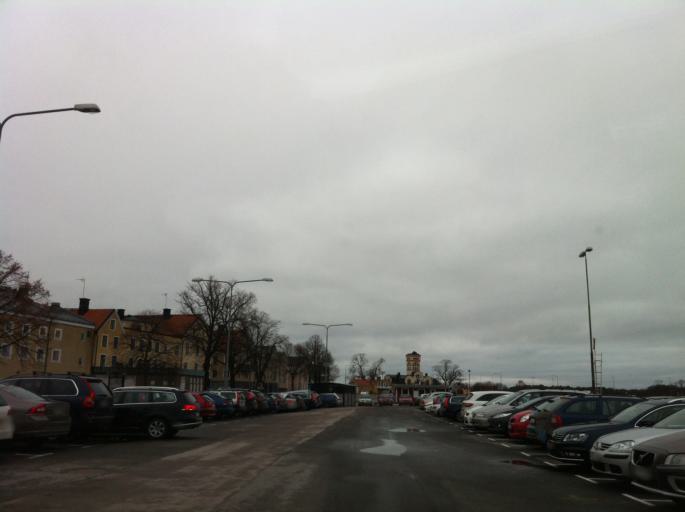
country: SE
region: Kalmar
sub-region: Vasterviks Kommun
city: Vaestervik
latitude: 57.7948
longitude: 16.6231
